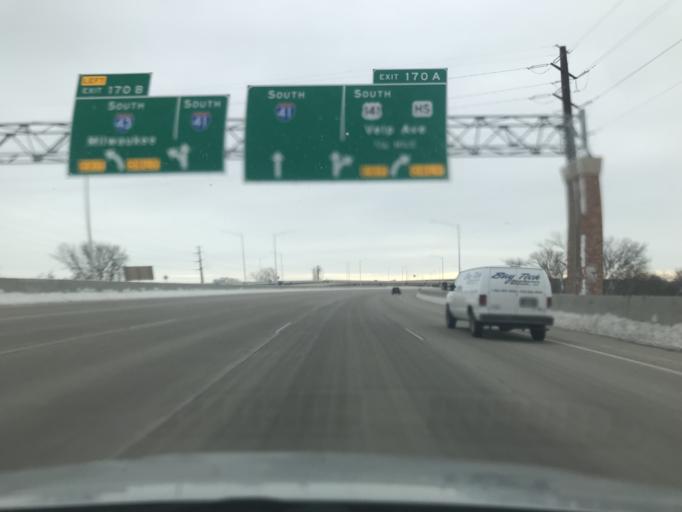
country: US
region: Wisconsin
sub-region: Brown County
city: Howard
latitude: 44.5680
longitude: -88.0487
